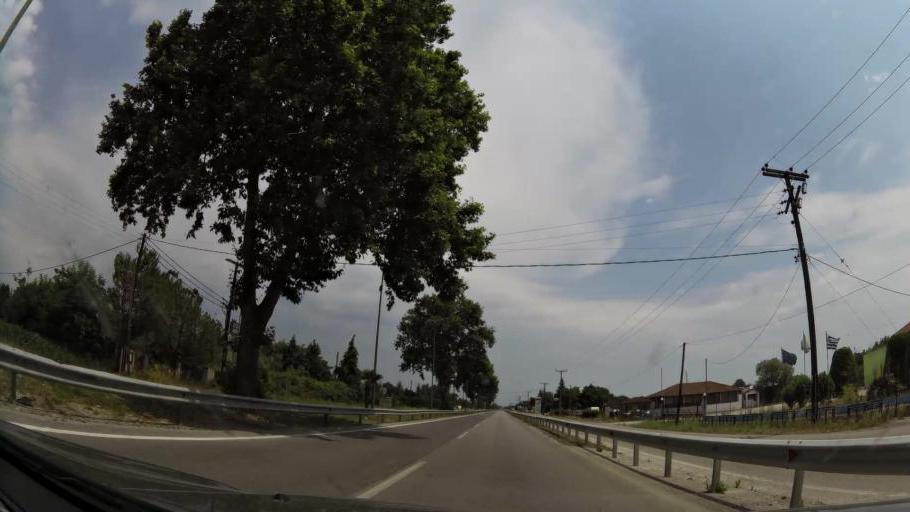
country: GR
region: Central Macedonia
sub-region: Nomos Pierias
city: Peristasi
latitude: 40.2721
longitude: 22.5585
